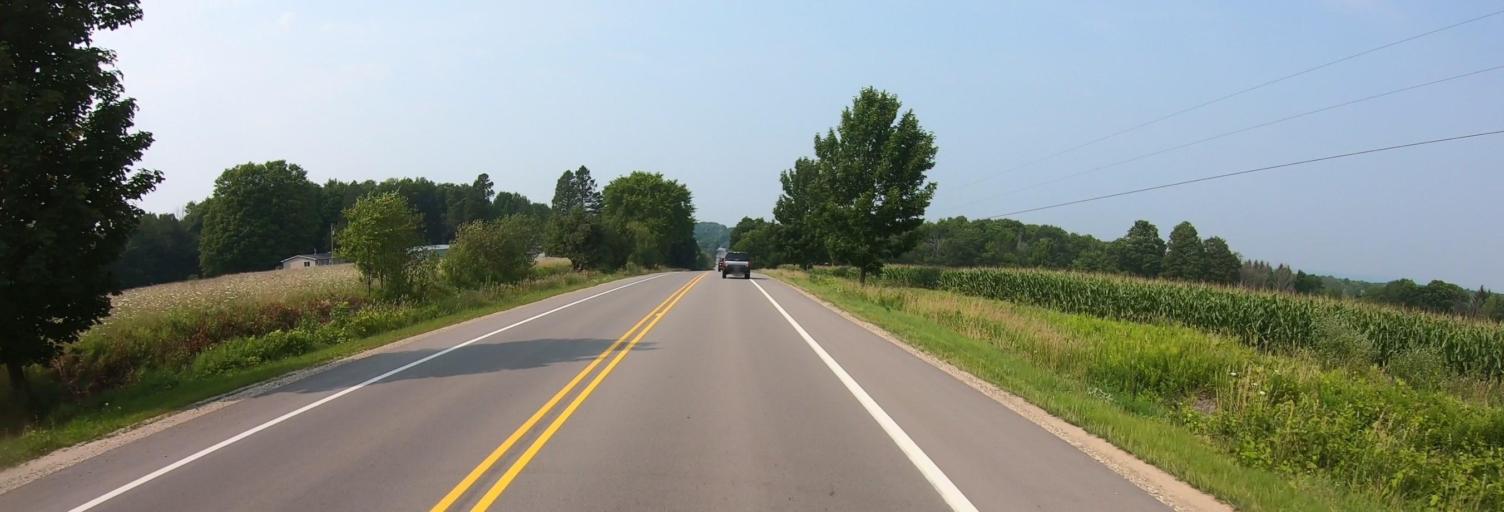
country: US
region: Michigan
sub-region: Charlevoix County
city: Charlevoix
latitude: 45.2445
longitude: -85.2611
